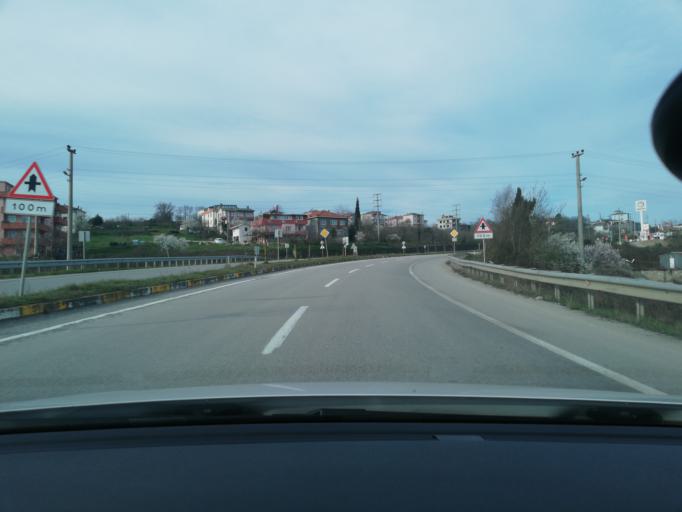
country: TR
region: Duzce
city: Akcakoca
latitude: 41.0833
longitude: 31.1465
